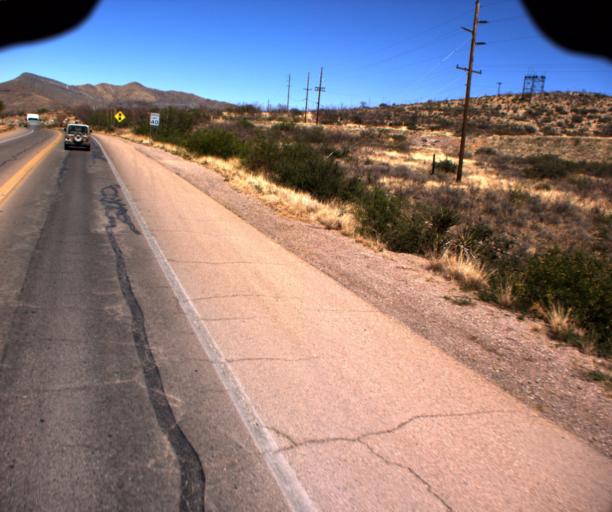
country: US
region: Arizona
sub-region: Cochise County
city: Bisbee
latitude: 31.4177
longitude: -109.8972
